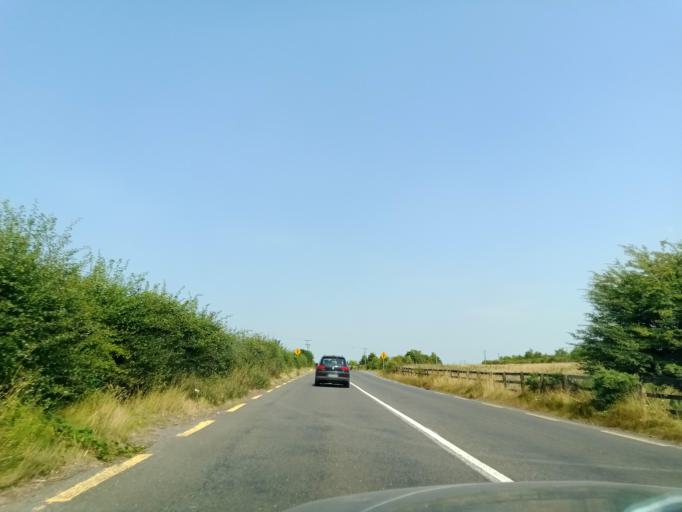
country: IE
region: Leinster
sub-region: Laois
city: Portlaoise
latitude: 53.0656
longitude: -7.2217
